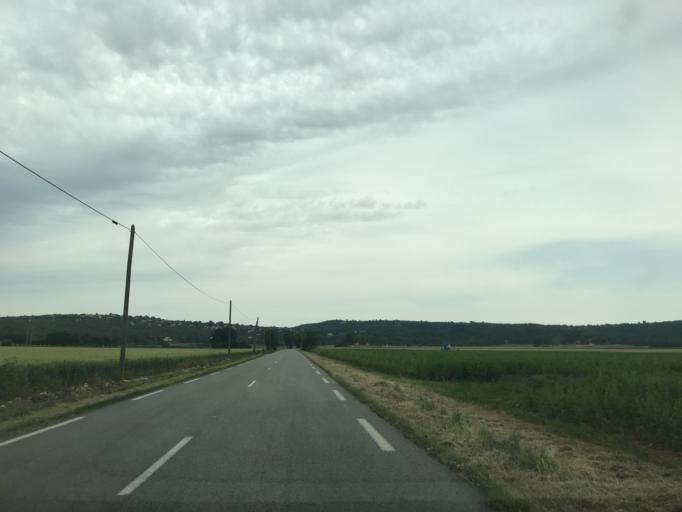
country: FR
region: Provence-Alpes-Cote d'Azur
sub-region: Departement du Var
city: Ginasservis
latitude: 43.6511
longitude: 5.8410
